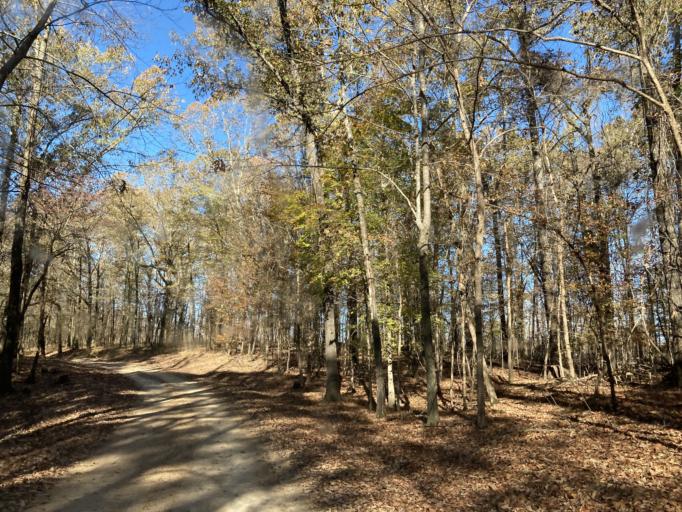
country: US
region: Mississippi
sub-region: Yazoo County
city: Yazoo City
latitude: 32.6727
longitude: -90.5066
